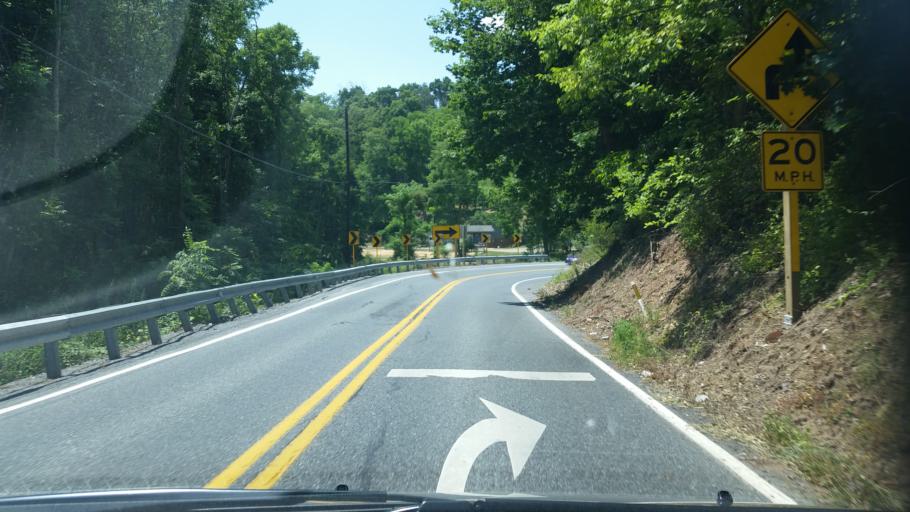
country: US
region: Pennsylvania
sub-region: Dauphin County
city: Hummelstown
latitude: 40.2896
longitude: -76.7095
